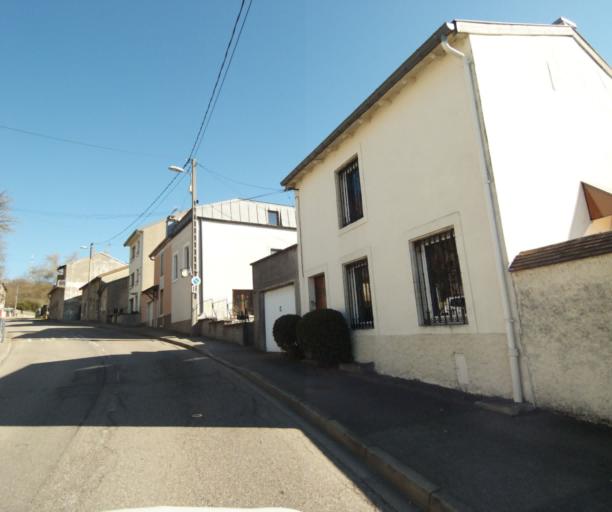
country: FR
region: Lorraine
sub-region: Departement de Meurthe-et-Moselle
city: Malzeville
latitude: 48.7075
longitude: 6.1915
